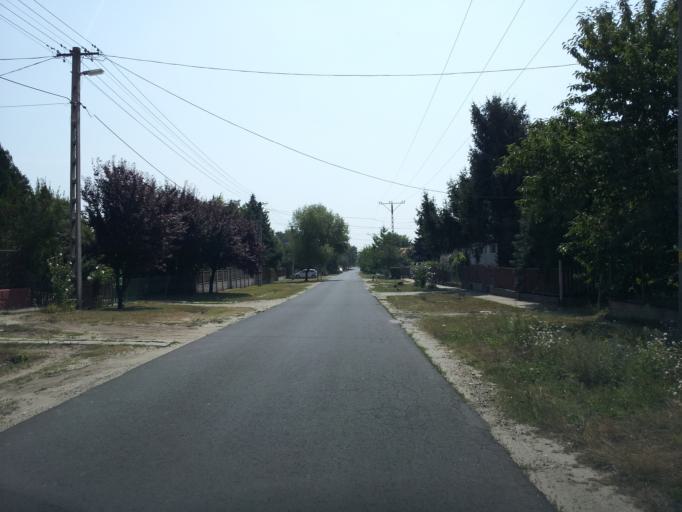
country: HU
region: Pest
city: Dunavarsany
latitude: 47.2775
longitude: 19.0737
